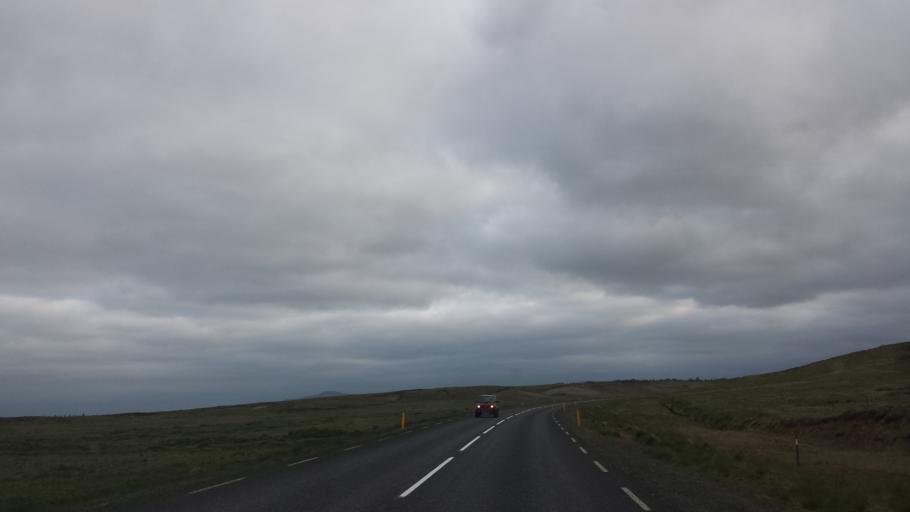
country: IS
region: South
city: Selfoss
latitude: 64.1309
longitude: -20.5829
